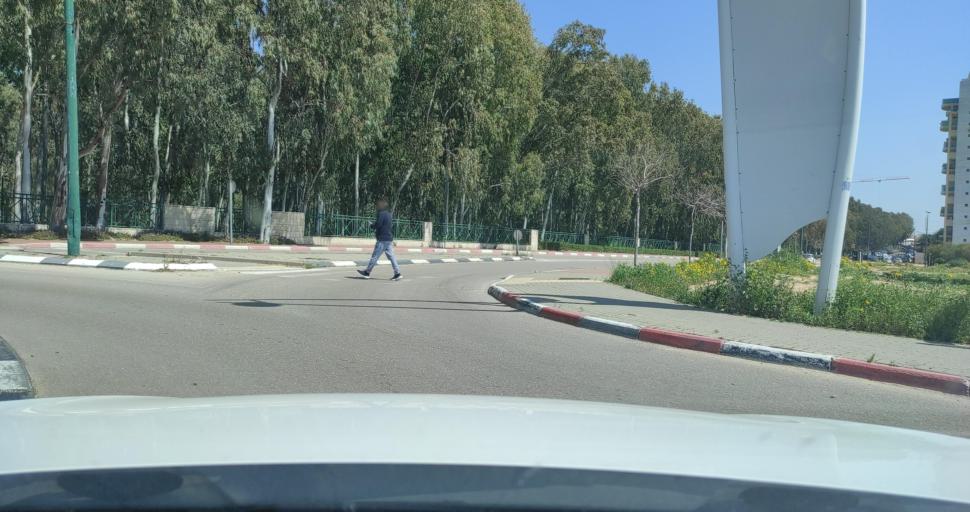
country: IL
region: Central District
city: Nordiyya
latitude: 32.3032
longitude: 34.8740
